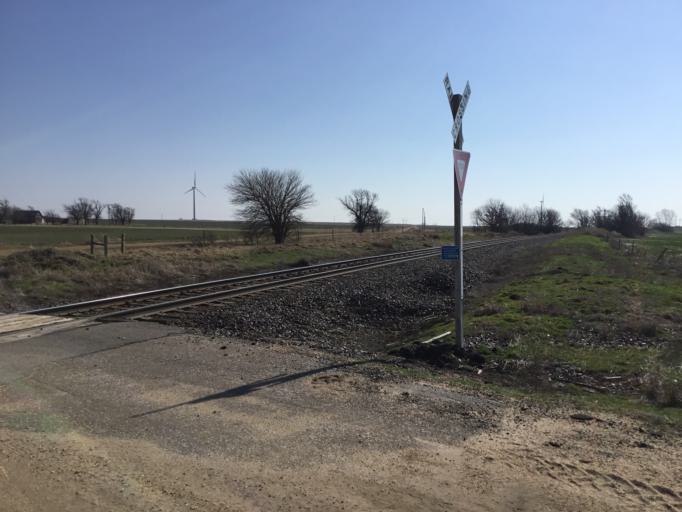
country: US
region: Kansas
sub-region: Ellsworth County
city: Ellsworth
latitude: 38.8126
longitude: -98.4192
